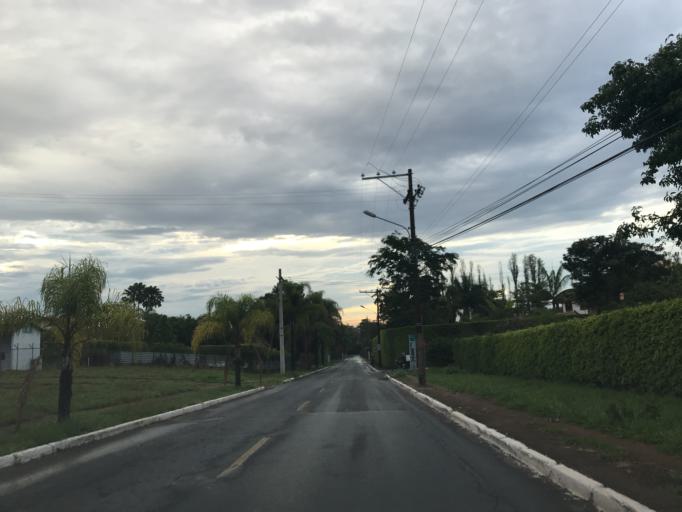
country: BR
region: Federal District
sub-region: Brasilia
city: Brasilia
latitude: -15.8538
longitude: -47.8529
